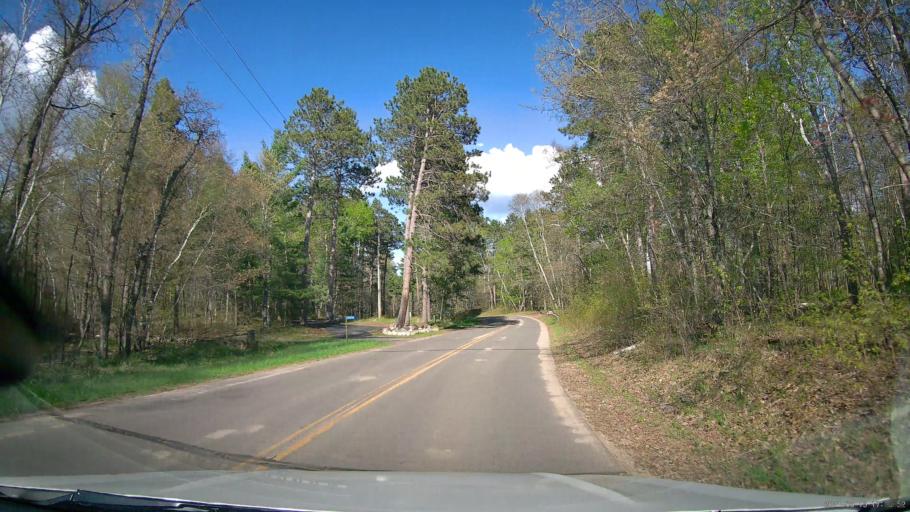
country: US
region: Minnesota
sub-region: Hubbard County
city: Park Rapids
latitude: 46.9915
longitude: -94.9639
